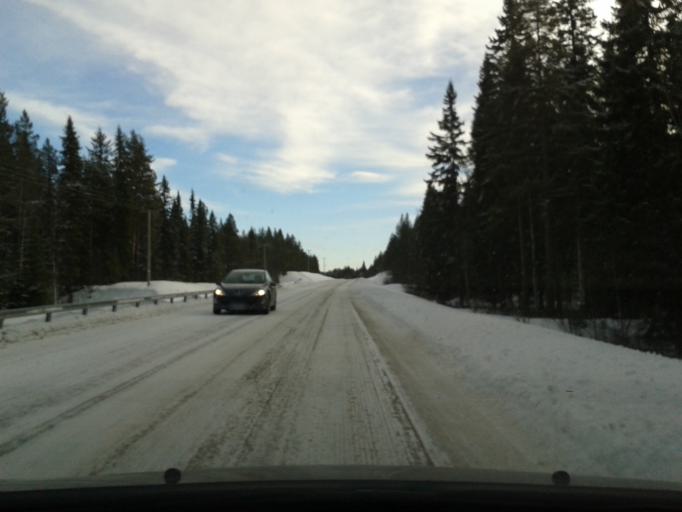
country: SE
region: Vaesterbotten
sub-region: Vilhelmina Kommun
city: Vilhelmina
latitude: 64.3789
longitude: 16.9005
